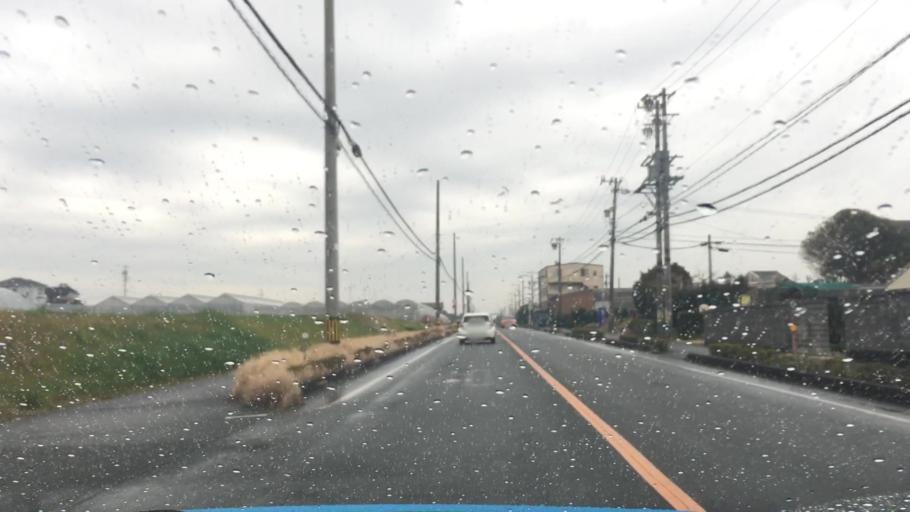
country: JP
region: Aichi
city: Toyohashi
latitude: 34.6935
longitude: 137.3907
